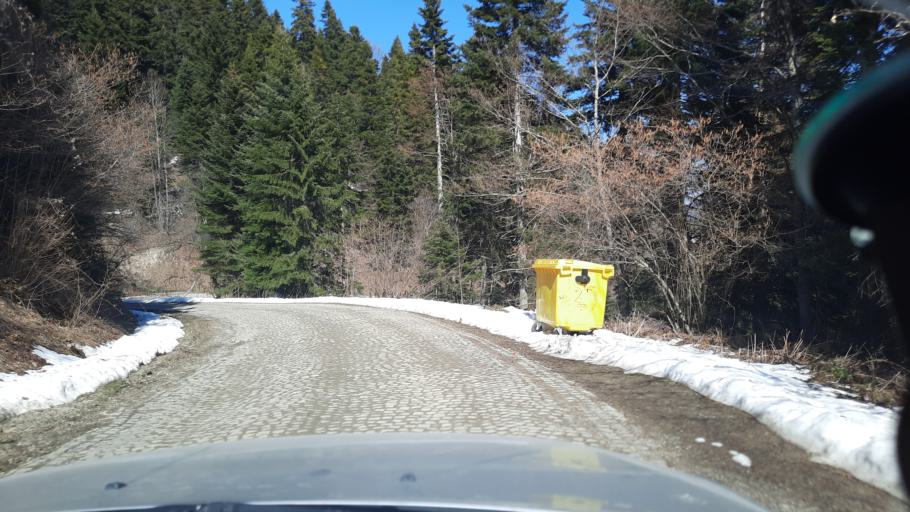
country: MK
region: Gostivar
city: Vrutok
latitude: 41.7008
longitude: 20.7523
